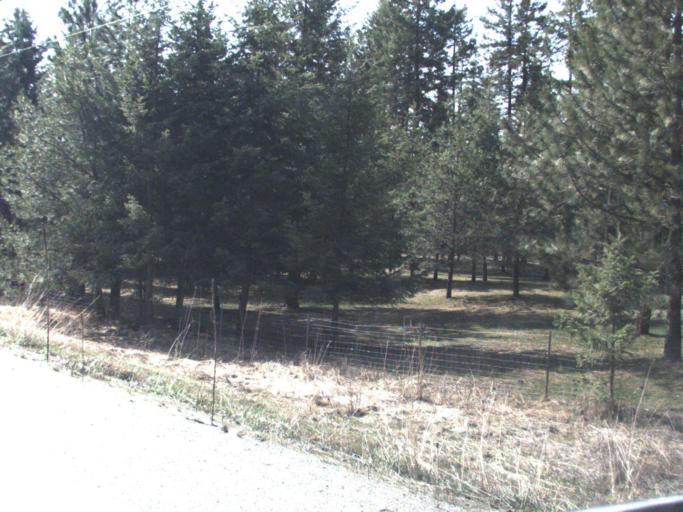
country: US
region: Washington
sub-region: Stevens County
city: Colville
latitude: 48.5255
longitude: -117.8180
